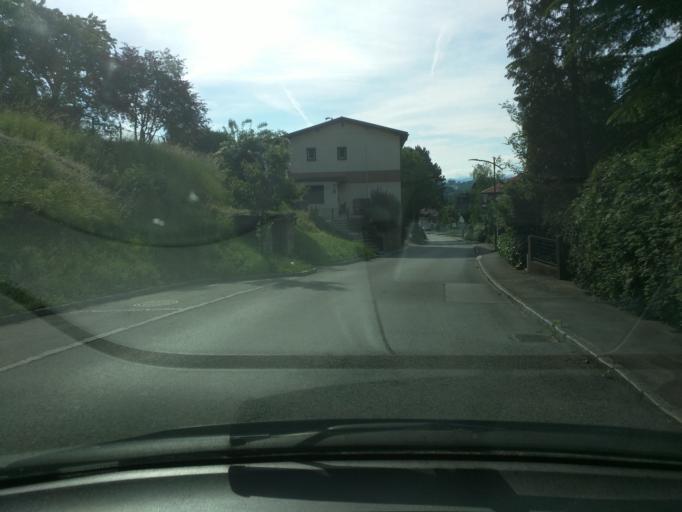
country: AT
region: Lower Austria
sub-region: Politischer Bezirk Melk
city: Petzenkirchen
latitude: 48.1479
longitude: 15.1493
